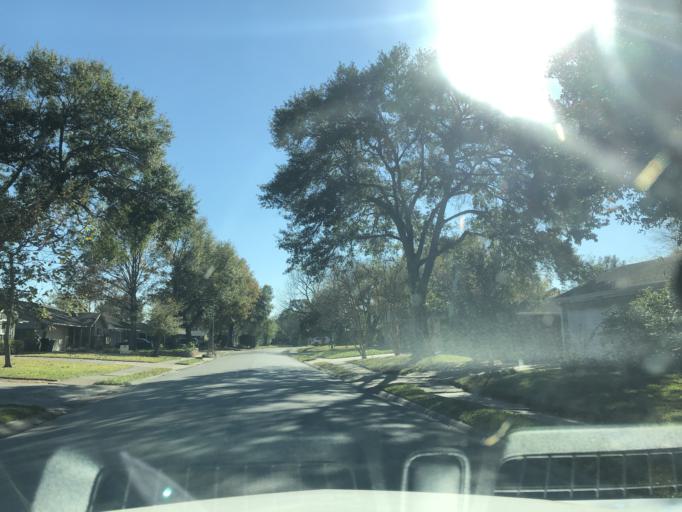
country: US
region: Texas
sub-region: Harris County
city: Bellaire
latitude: 29.6946
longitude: -95.5008
